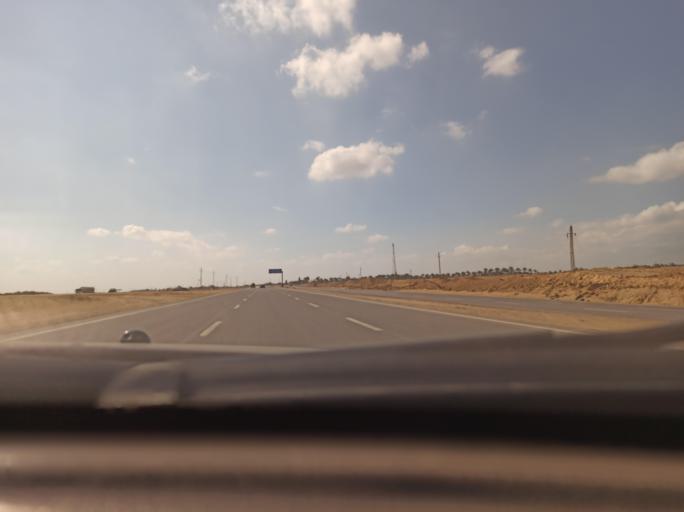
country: EG
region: Muhafazat al Fayyum
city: Al Wasitah
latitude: 29.3739
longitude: 31.0848
